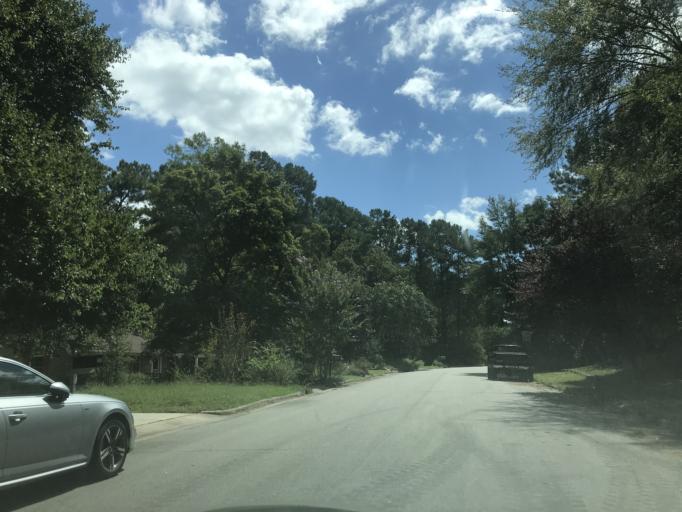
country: US
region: North Carolina
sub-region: Orange County
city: Chapel Hill
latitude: 35.9281
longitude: -79.0144
